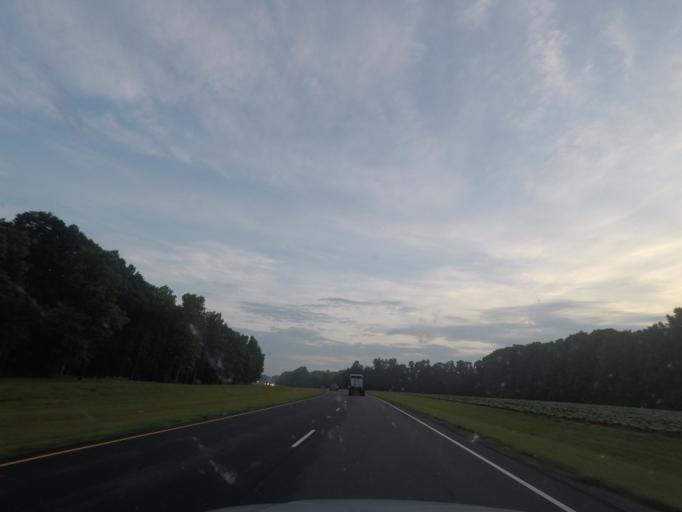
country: US
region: North Carolina
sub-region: Person County
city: Roxboro
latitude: 36.2639
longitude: -78.9432
